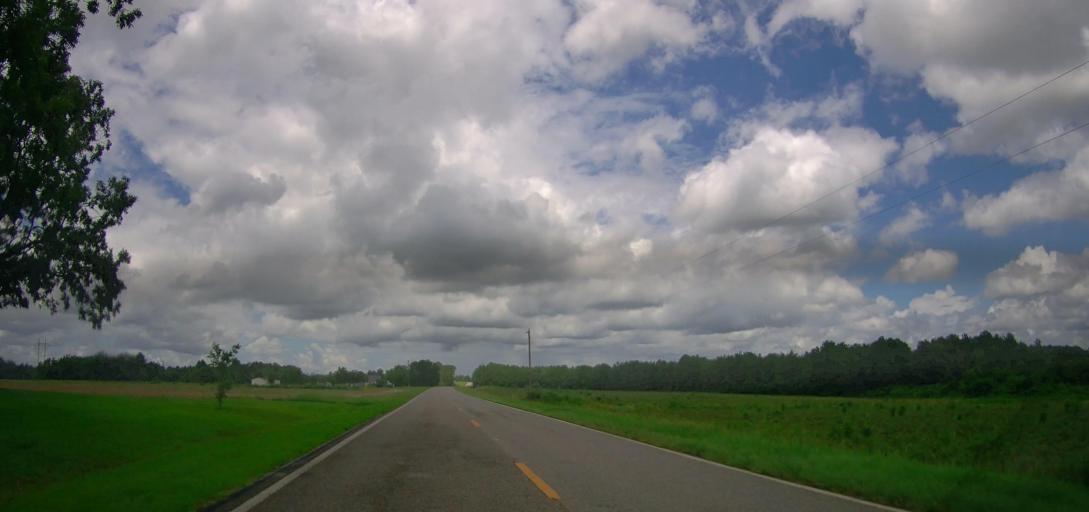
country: US
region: Georgia
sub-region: Wilcox County
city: Rochelle
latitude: 31.8812
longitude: -83.5570
